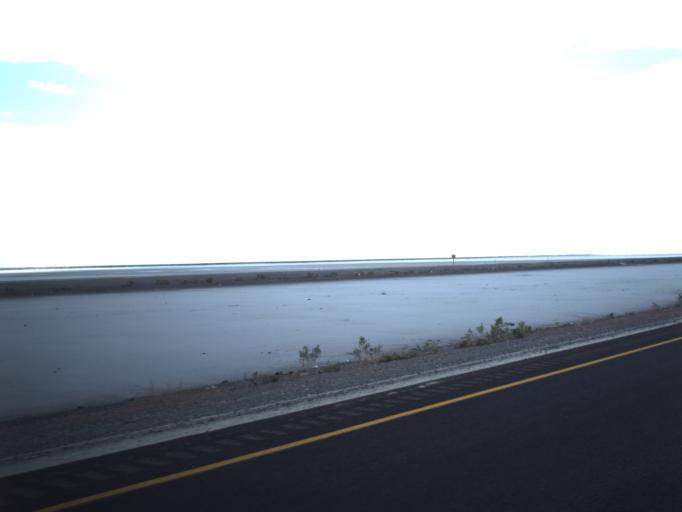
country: US
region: Utah
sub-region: Tooele County
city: Wendover
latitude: 40.7320
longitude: -113.5479
